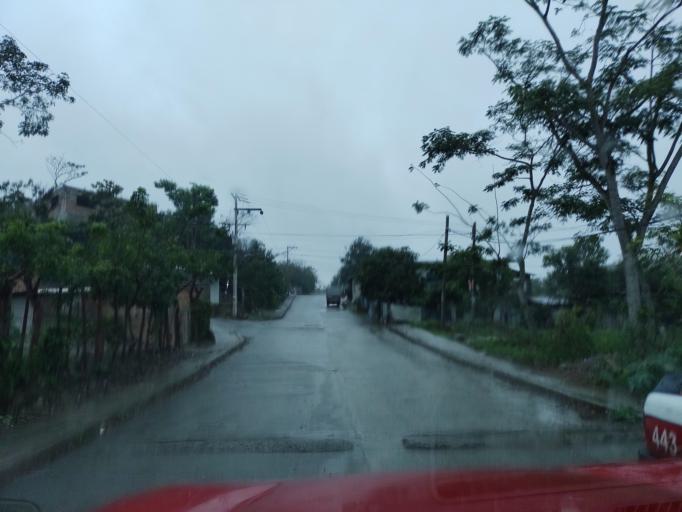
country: MX
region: Veracruz
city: Papantla de Olarte
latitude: 20.4361
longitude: -97.3378
